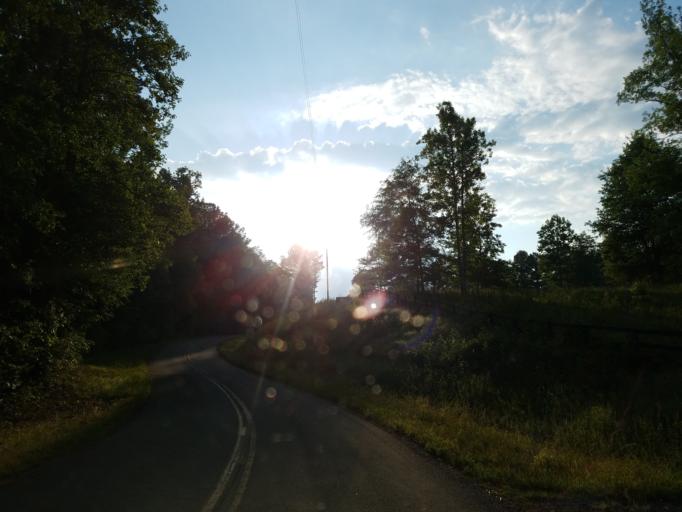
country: US
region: Georgia
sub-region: Cherokee County
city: Ball Ground
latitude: 34.2997
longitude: -84.3825
